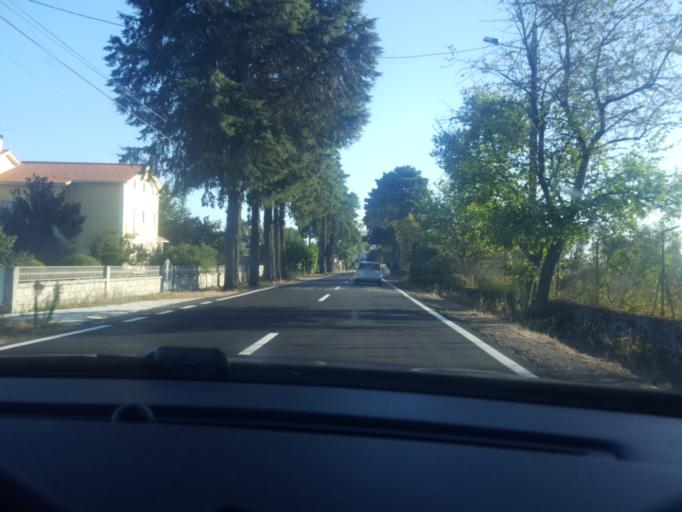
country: PT
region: Viseu
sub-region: Mangualde
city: Mangualde
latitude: 40.5820
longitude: -7.8060
